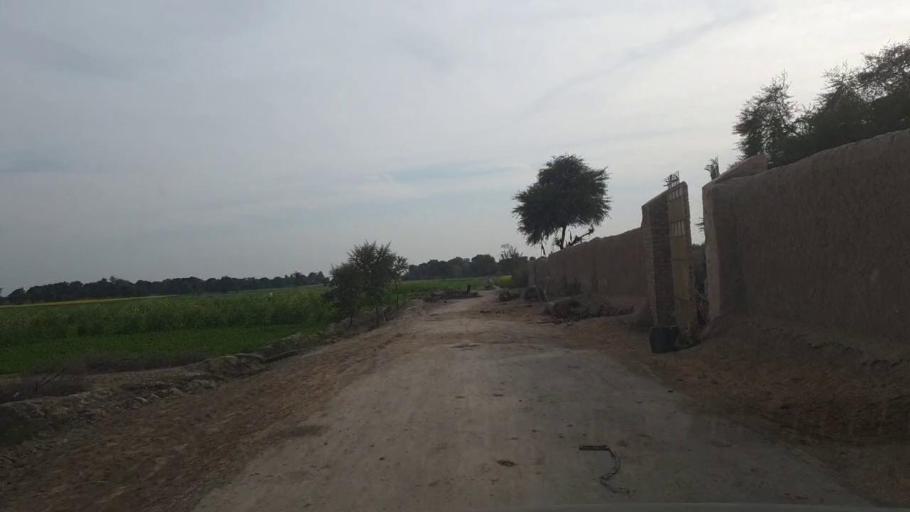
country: PK
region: Sindh
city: Shahpur Chakar
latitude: 26.1106
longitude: 68.5278
